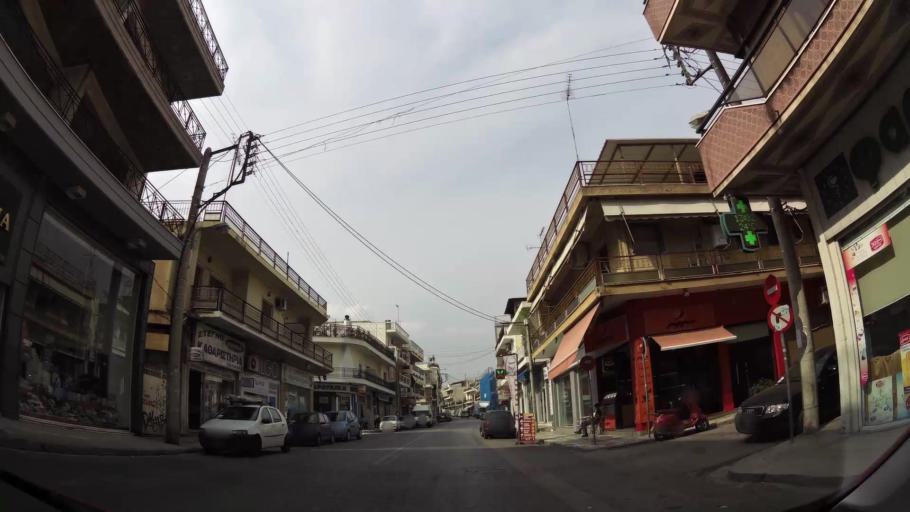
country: GR
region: Attica
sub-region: Nomarchia Athinas
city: Peristeri
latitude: 38.0123
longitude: 23.6848
